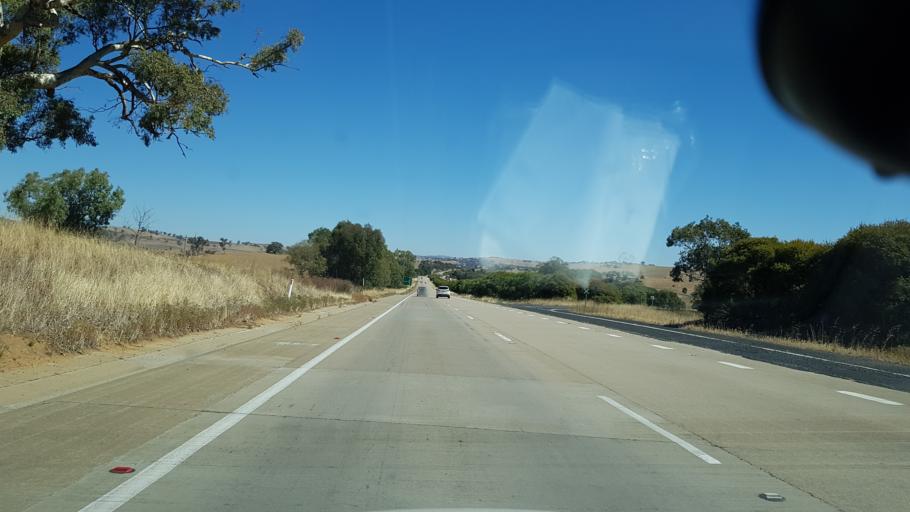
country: AU
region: New South Wales
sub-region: Gundagai
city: Gundagai
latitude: -34.8174
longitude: 148.3895
